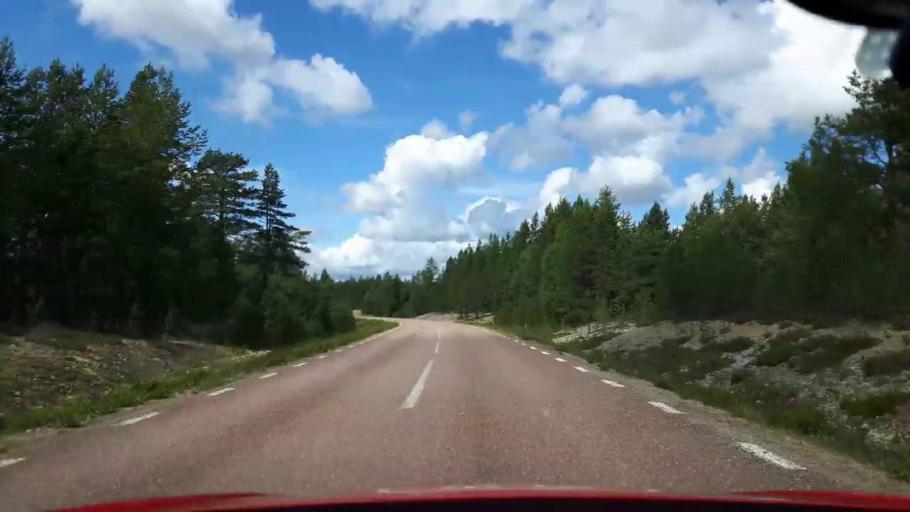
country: SE
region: Dalarna
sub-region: Alvdalens Kommun
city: AElvdalen
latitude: 61.8049
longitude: 13.6531
